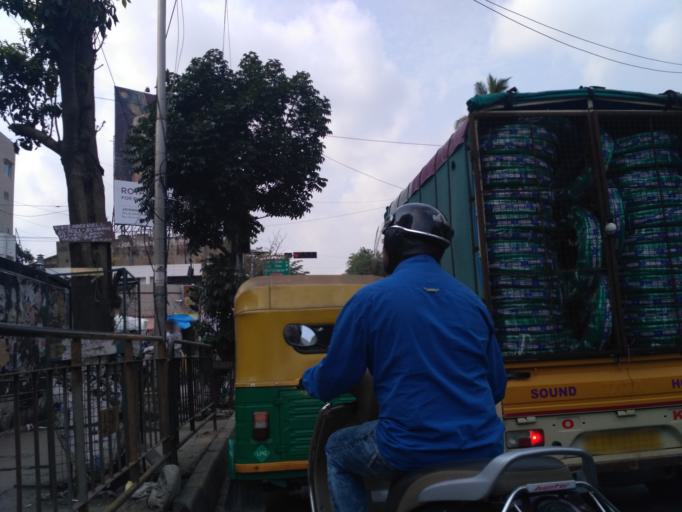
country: IN
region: Karnataka
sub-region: Bangalore Urban
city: Bangalore
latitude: 12.9613
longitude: 77.5840
